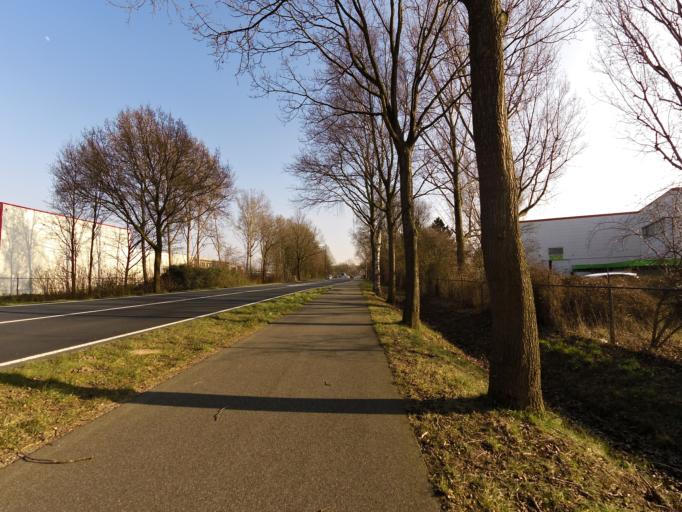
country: DE
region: North Rhine-Westphalia
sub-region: Regierungsbezirk Dusseldorf
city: Emmerich
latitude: 51.8440
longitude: 6.2722
